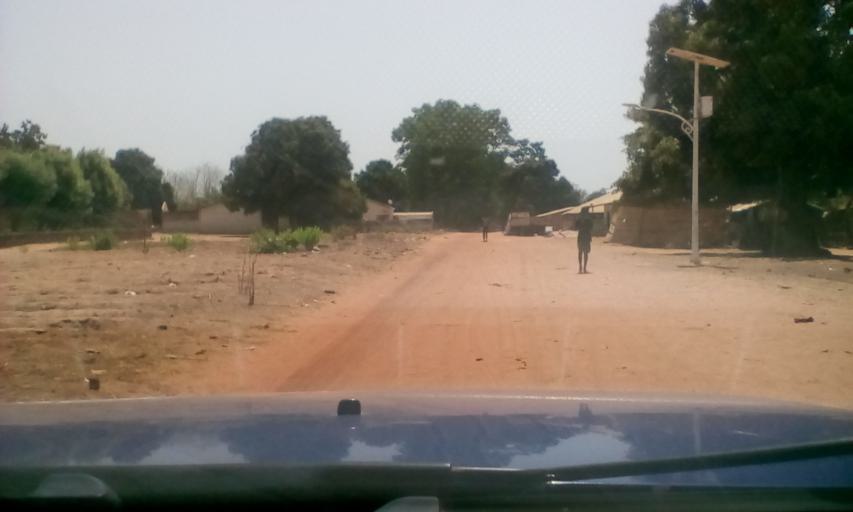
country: GW
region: Oio
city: Bissora
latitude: 12.4407
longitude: -15.5333
